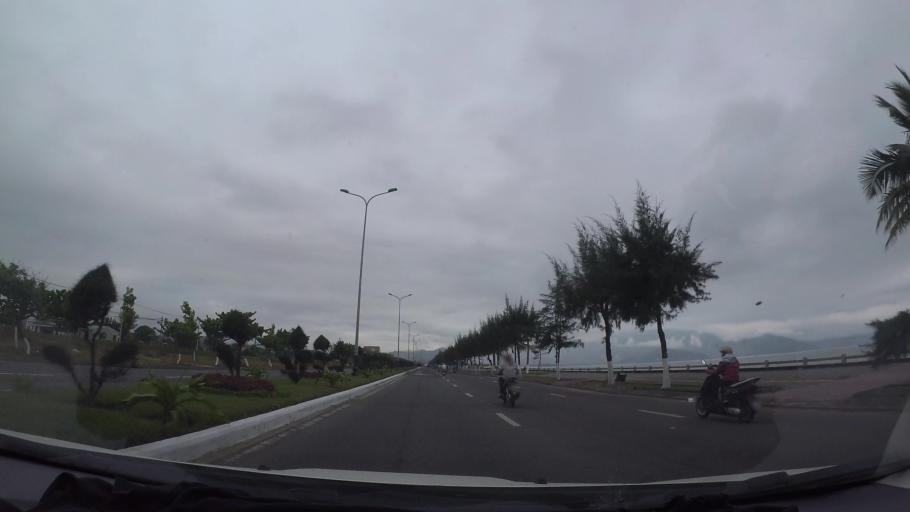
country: VN
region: Da Nang
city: Lien Chieu
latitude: 16.0863
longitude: 108.1581
